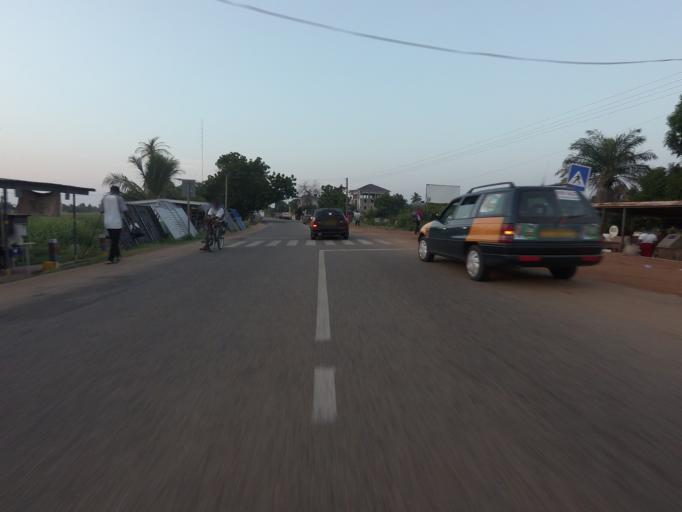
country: GH
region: Volta
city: Keta
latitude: 5.8779
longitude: 0.9814
